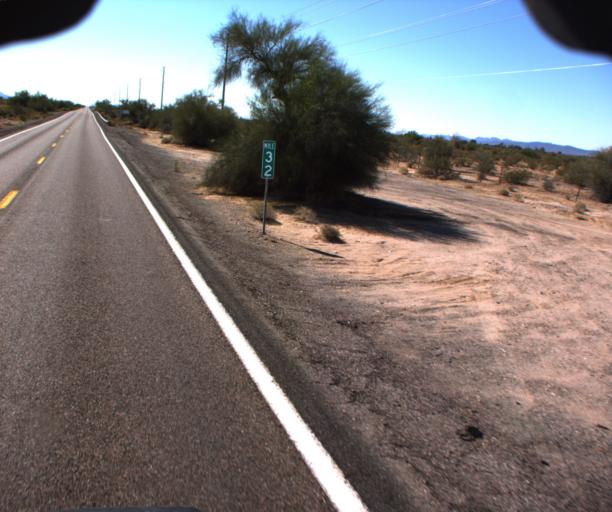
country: US
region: Arizona
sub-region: La Paz County
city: Salome
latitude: 33.8814
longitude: -113.9466
